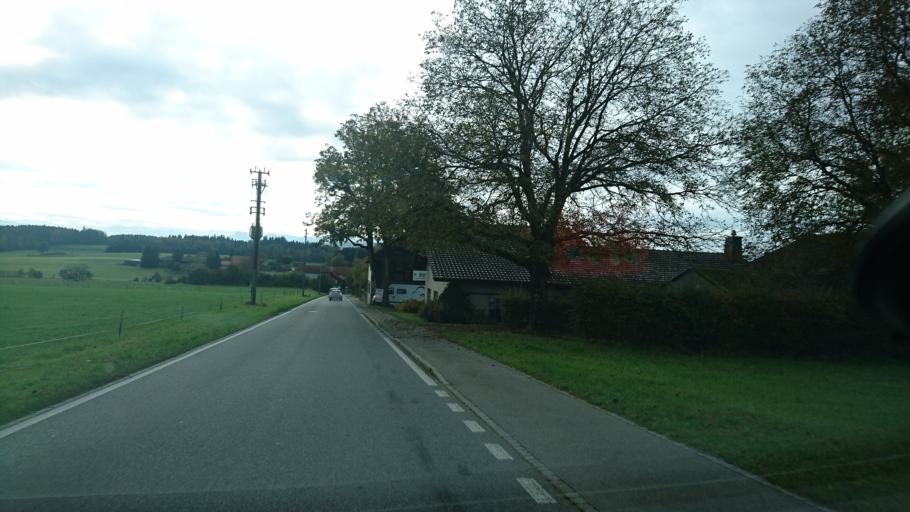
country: CH
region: Bern
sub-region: Bern-Mittelland District
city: Kirchlindach
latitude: 46.9962
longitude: 7.4115
